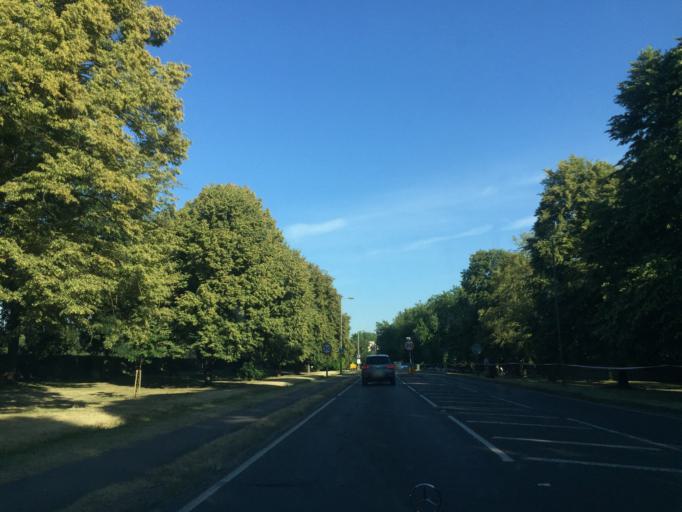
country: GB
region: England
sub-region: Oxfordshire
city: Henley on Thames
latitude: 51.5462
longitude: -0.9140
